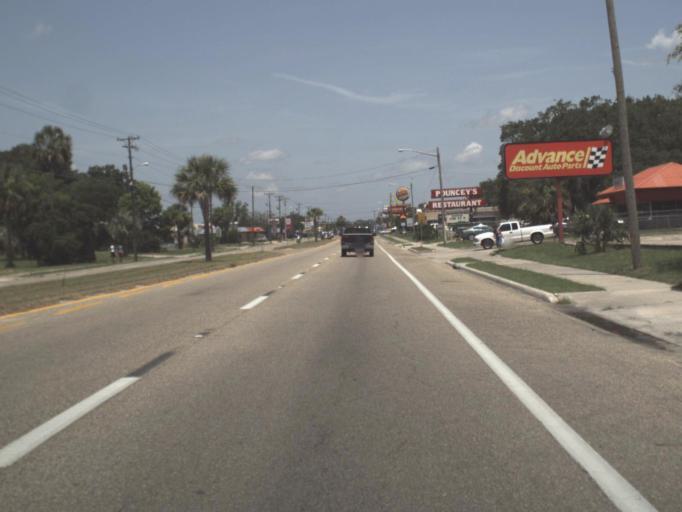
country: US
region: Florida
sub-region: Taylor County
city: Perry
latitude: 30.0952
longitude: -83.5800
